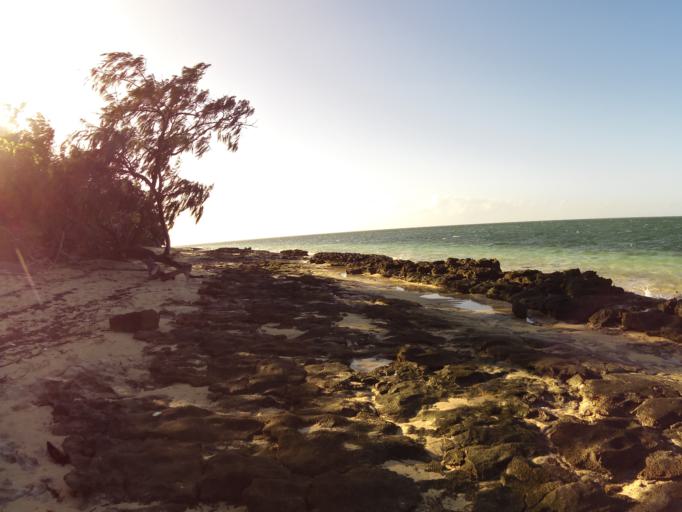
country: AU
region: Queensland
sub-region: Cairns
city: Yorkeys Knob
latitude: -16.7607
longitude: 145.9741
